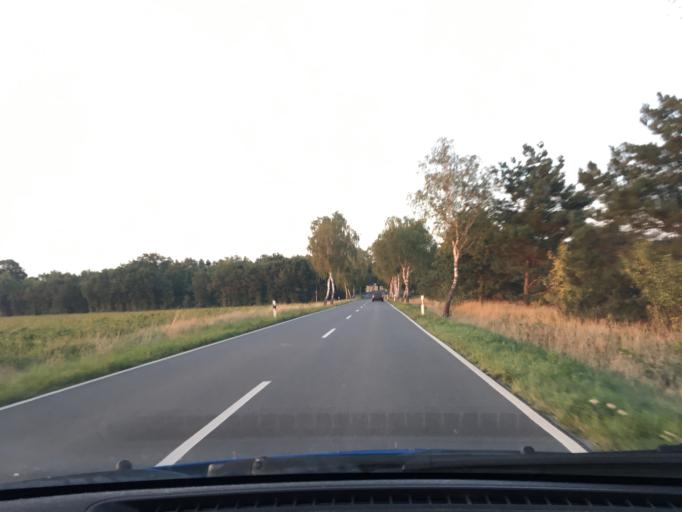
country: DE
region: Lower Saxony
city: Karwitz
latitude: 53.1359
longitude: 10.9730
